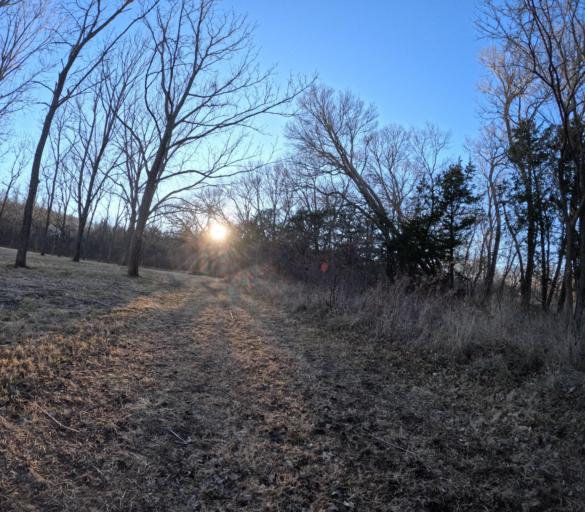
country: US
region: Kansas
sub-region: Riley County
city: Ogden
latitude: 39.2035
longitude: -96.6841
